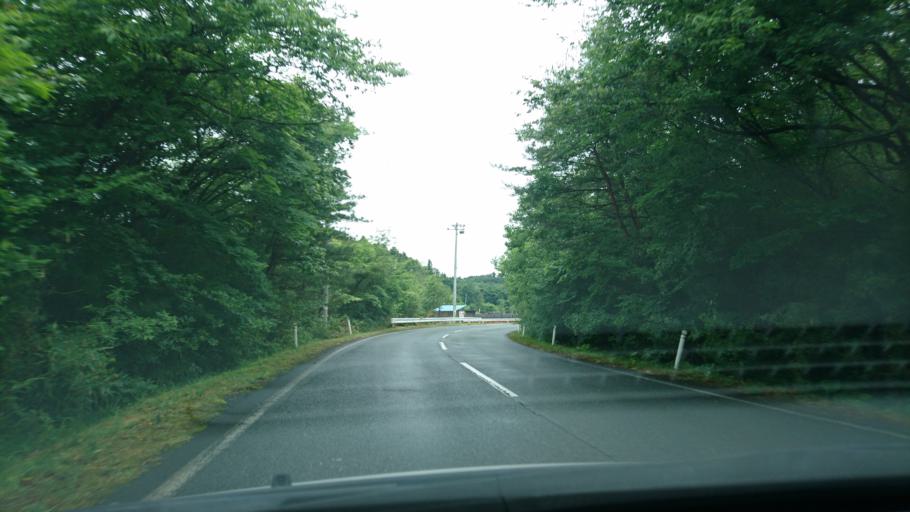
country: JP
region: Iwate
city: Ichinoseki
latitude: 38.8957
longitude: 141.1526
